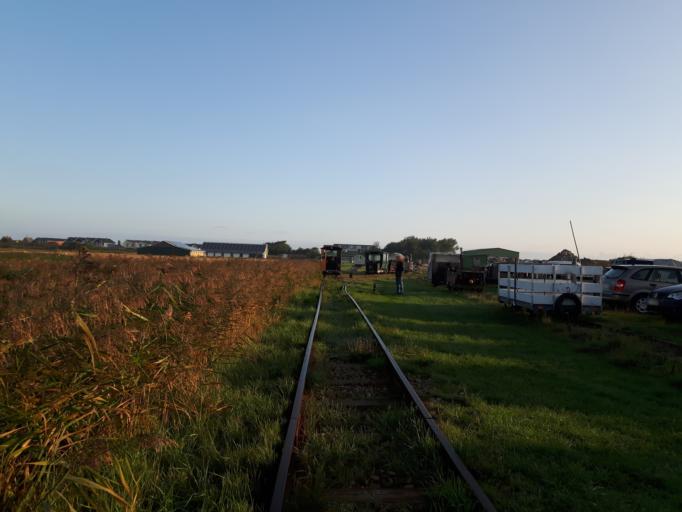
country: DE
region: Schleswig-Holstein
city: Dagebull
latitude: 54.7257
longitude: 8.7000
